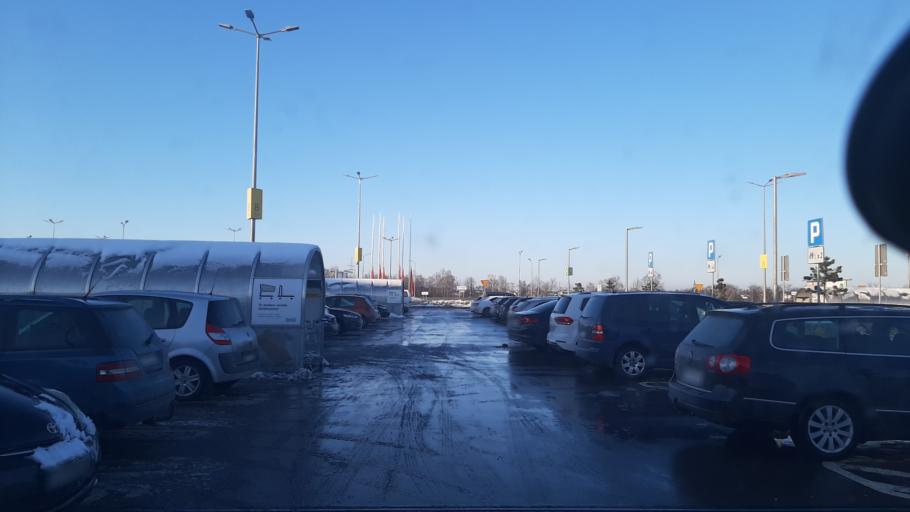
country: PL
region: Lublin Voivodeship
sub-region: Powiat lubelski
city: Lublin
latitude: 51.2828
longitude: 22.5725
